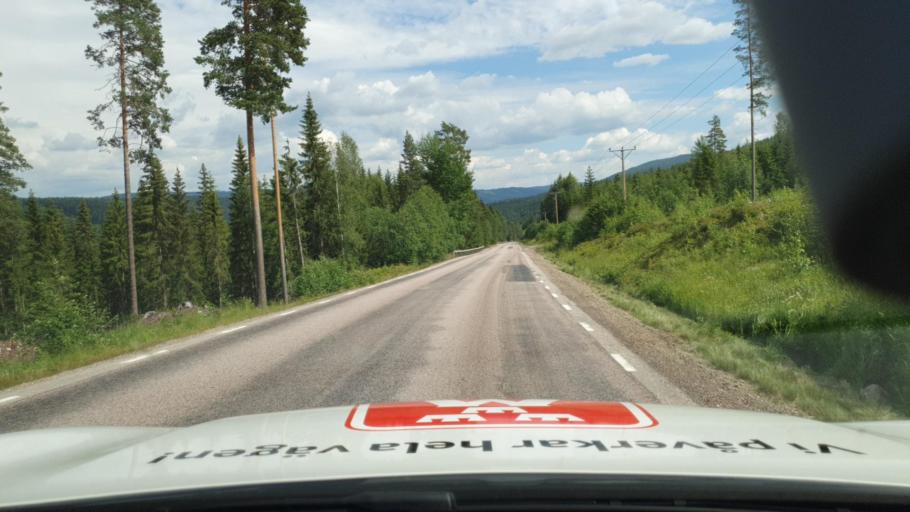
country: SE
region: Vaermland
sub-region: Torsby Kommun
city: Torsby
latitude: 60.7527
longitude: 12.7569
